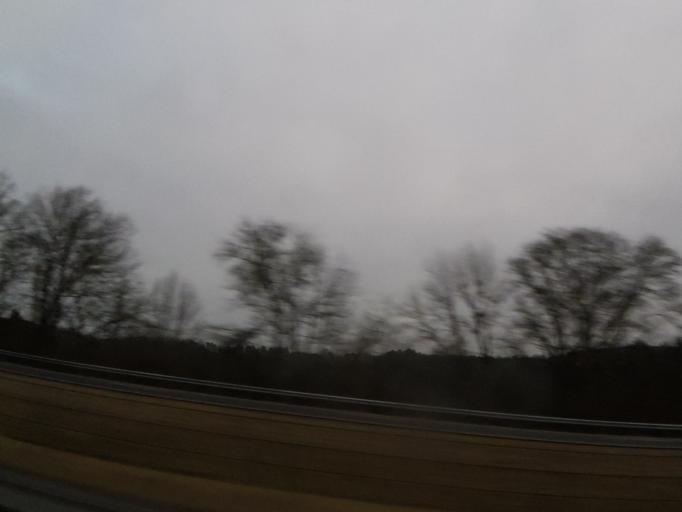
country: US
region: Alabama
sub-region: Cullman County
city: Cullman
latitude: 34.1808
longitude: -86.8773
